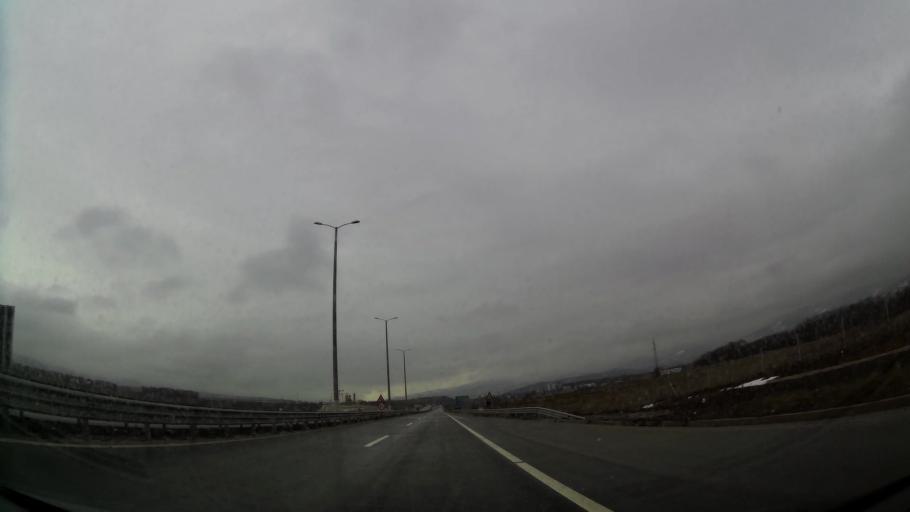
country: XK
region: Ferizaj
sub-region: Komuna e Kacanikut
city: Kacanik
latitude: 42.2857
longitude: 21.2082
